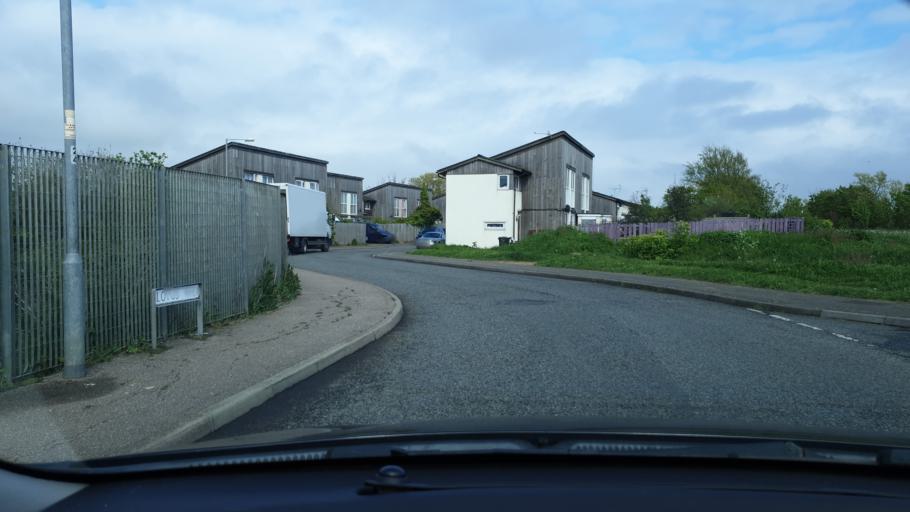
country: GB
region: England
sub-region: Essex
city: Saint Osyth
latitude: 51.7749
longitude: 1.1042
